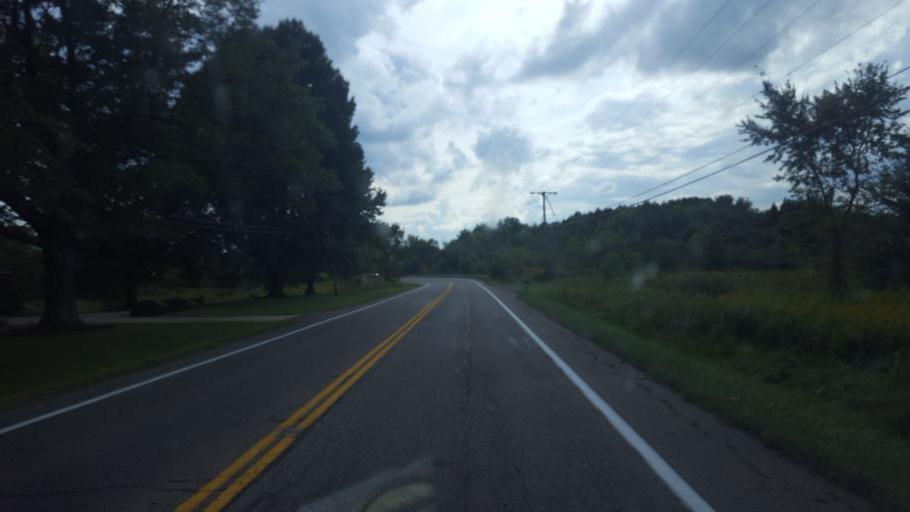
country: US
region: Ohio
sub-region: Portage County
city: Ravenna
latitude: 41.0628
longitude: -81.2464
